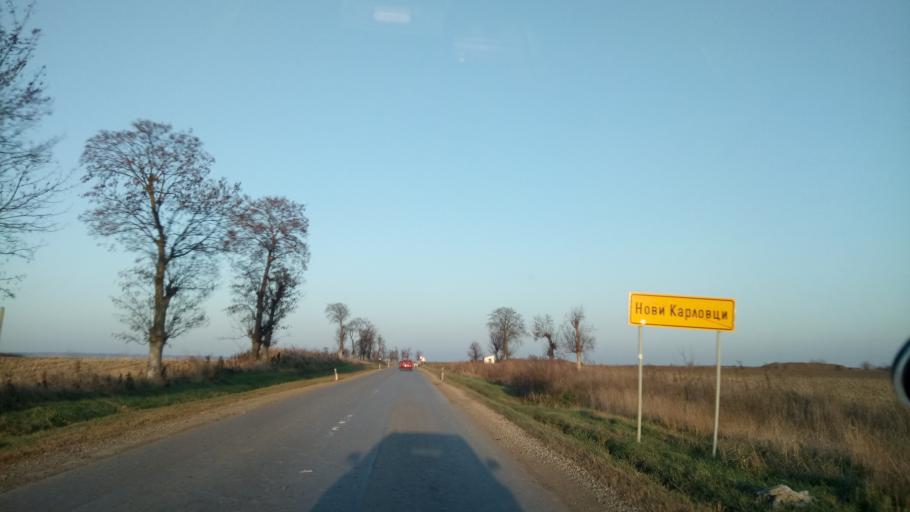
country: RS
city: Novi Karlovci
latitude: 45.0847
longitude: 20.1843
